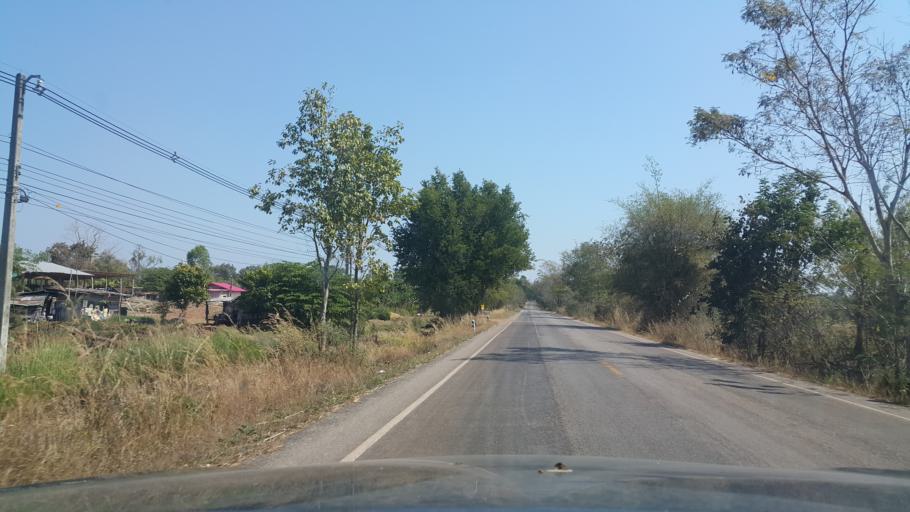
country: TH
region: Changwat Udon Thani
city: Ban Dung
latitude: 17.6094
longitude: 103.3135
